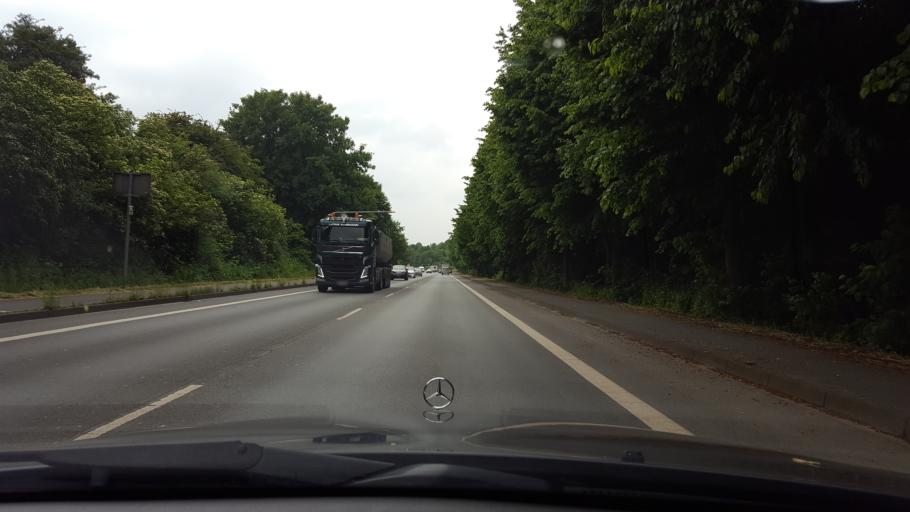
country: DE
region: North Rhine-Westphalia
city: Oer-Erkenschwick
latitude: 51.6154
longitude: 7.3170
